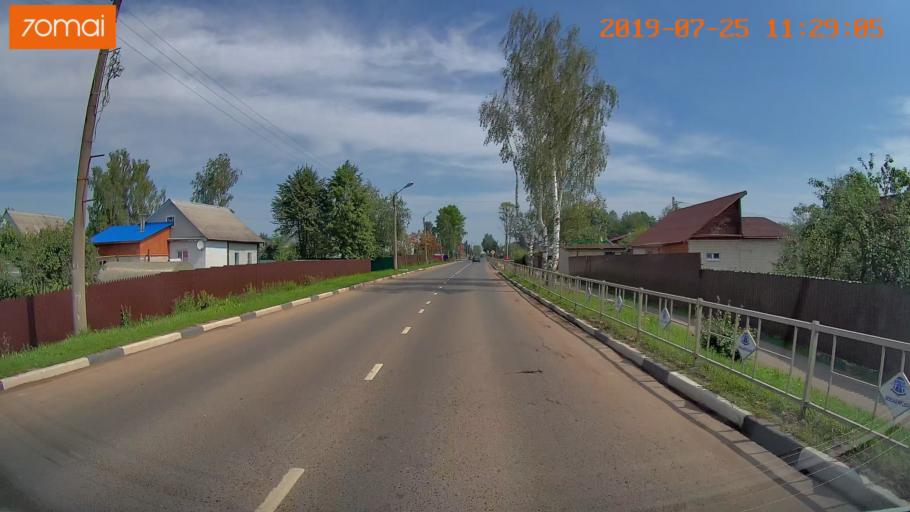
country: RU
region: Ivanovo
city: Privolzhsk
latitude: 57.3828
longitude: 41.3009
